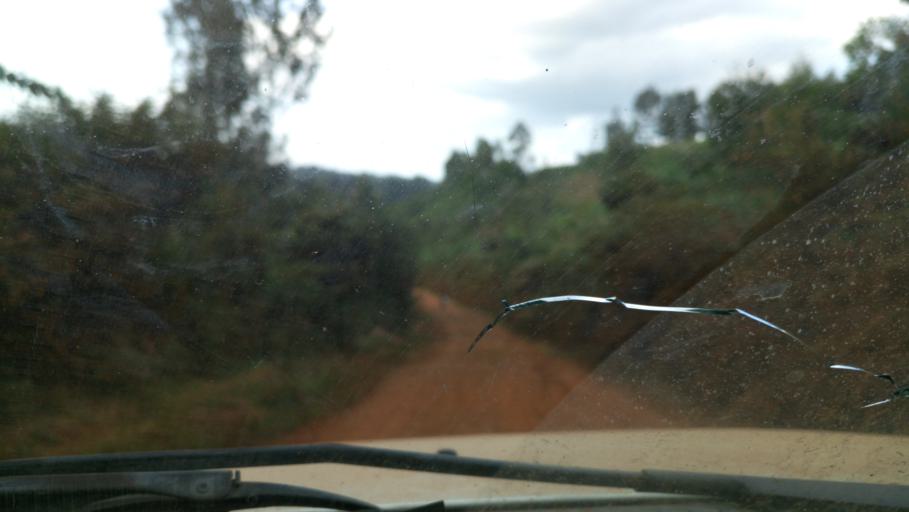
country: KE
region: Murang'a District
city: Kangema
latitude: -0.8688
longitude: 36.9515
